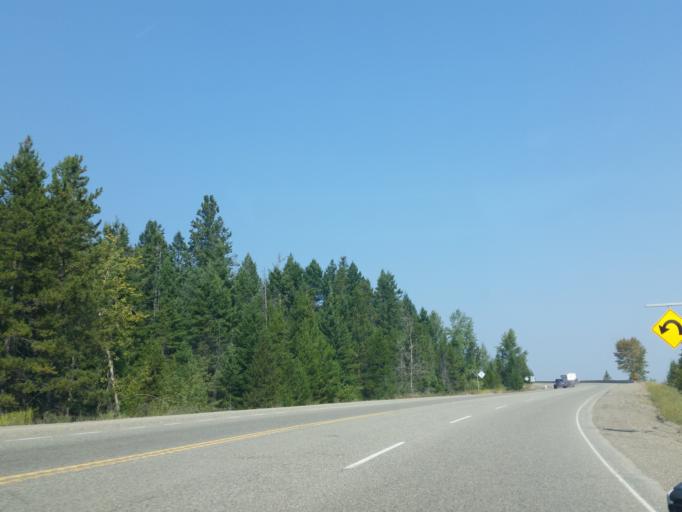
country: CA
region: British Columbia
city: Princeton
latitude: 49.3590
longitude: -120.5622
